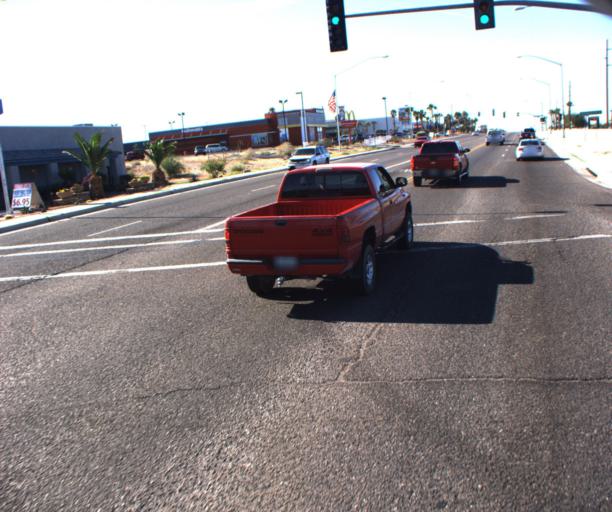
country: US
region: Arizona
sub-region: Mohave County
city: Bullhead City
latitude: 35.1074
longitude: -114.5981
